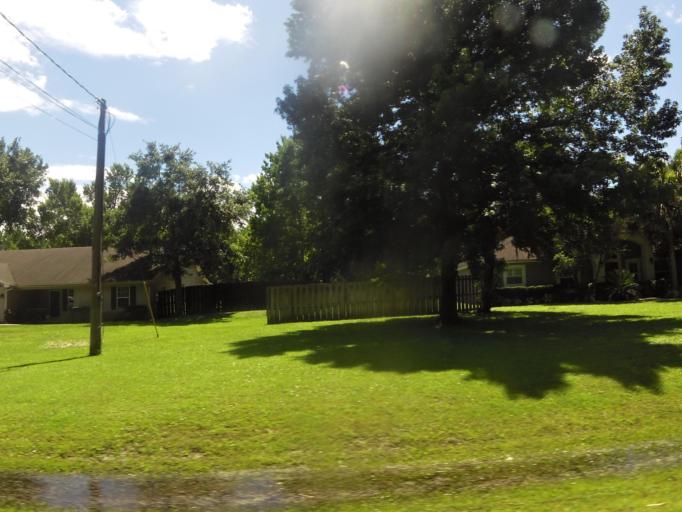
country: US
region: Georgia
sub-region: Camden County
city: St. Marys
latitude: 30.6789
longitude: -81.5333
